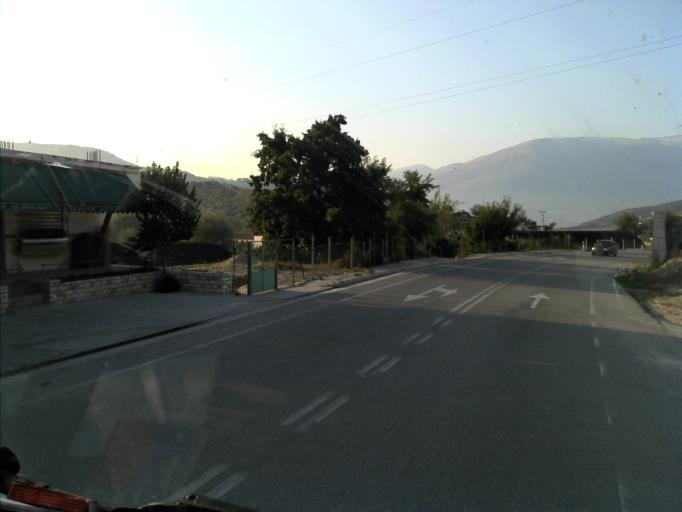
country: AL
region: Gjirokaster
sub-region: Rrethi i Tepelenes
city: Krahes
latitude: 40.4297
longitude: 19.8531
